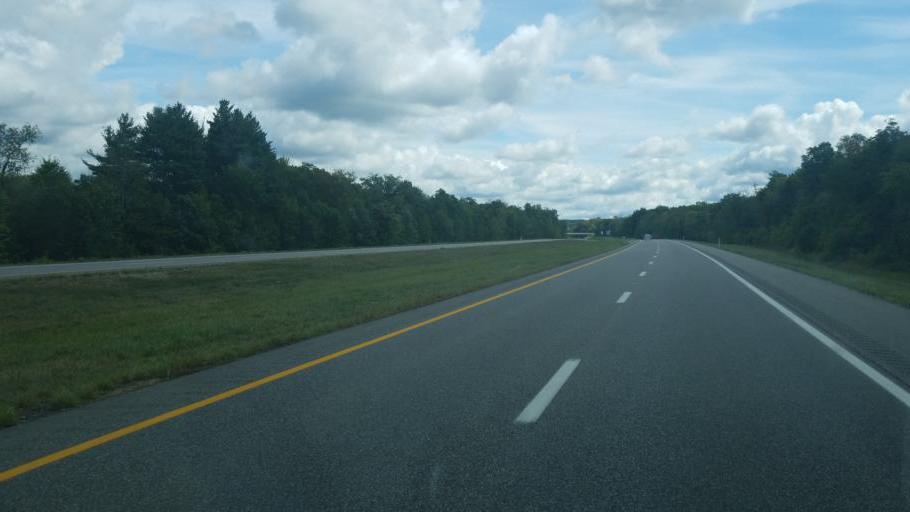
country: US
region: Ohio
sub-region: Geauga County
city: Bainbridge
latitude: 41.3810
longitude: -81.2869
